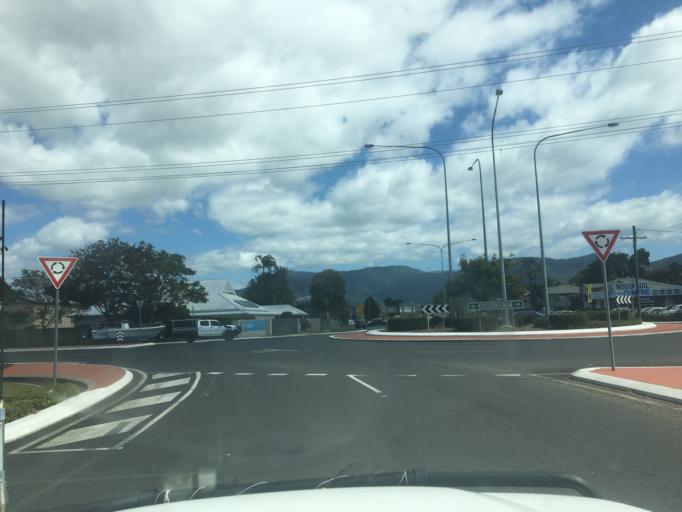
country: AU
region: Queensland
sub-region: Cairns
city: Cairns
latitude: -16.9332
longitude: 145.7612
